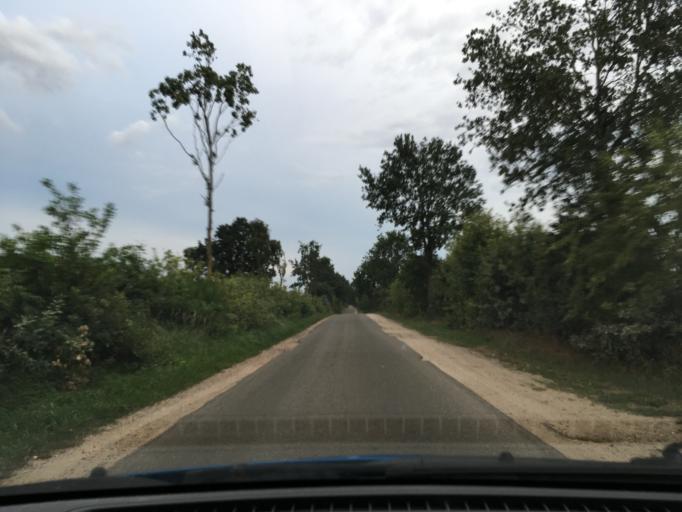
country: DE
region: Schleswig-Holstein
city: Lanze
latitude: 53.4095
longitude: 10.6067
